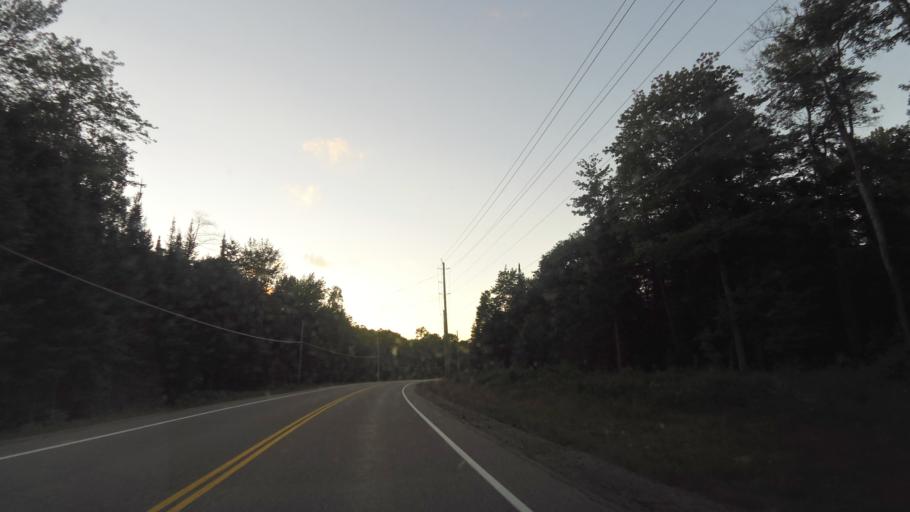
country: CA
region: Ontario
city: Bancroft
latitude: 45.0345
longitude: -78.4135
